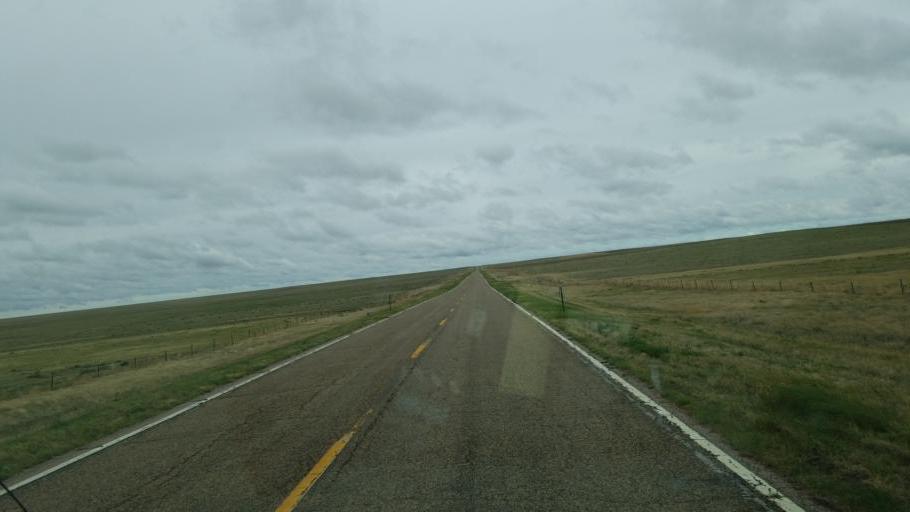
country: US
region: Colorado
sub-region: Lincoln County
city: Hugo
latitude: 38.8500
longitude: -103.4240
